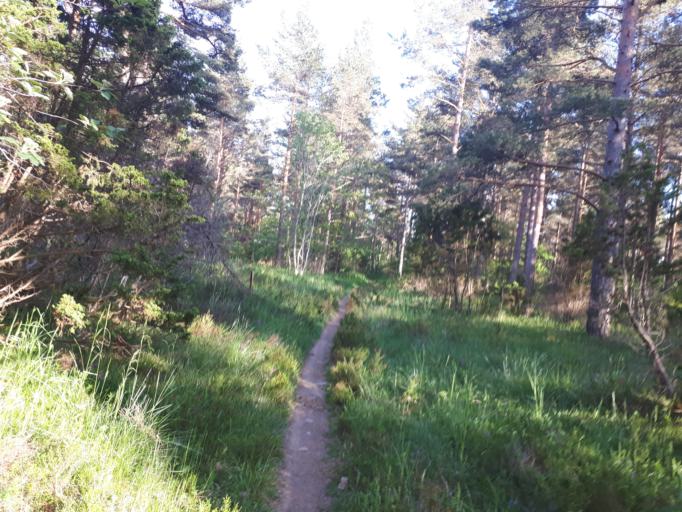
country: SE
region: Gotland
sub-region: Gotland
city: Visby
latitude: 57.6064
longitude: 18.2972
